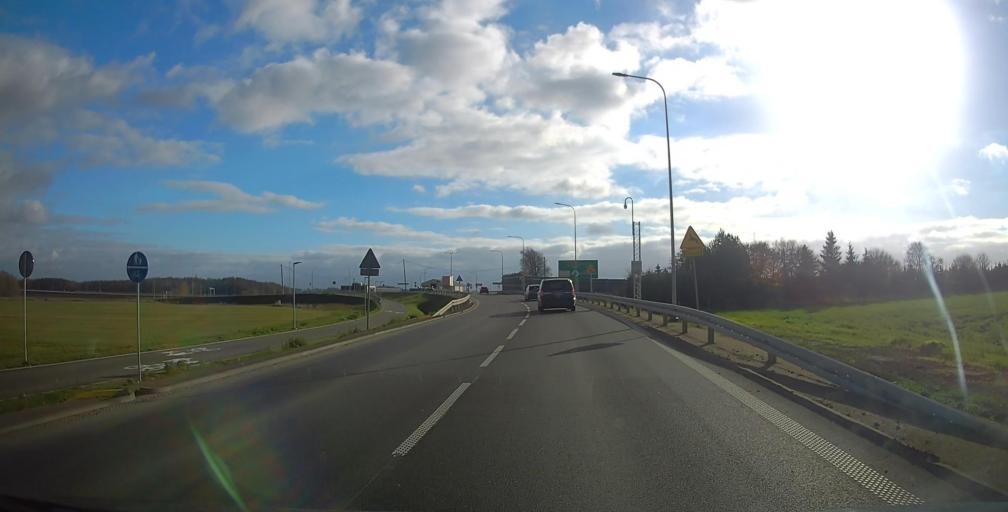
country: PL
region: Warmian-Masurian Voivodeship
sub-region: Powiat elcki
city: Elk
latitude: 53.7605
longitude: 22.3378
